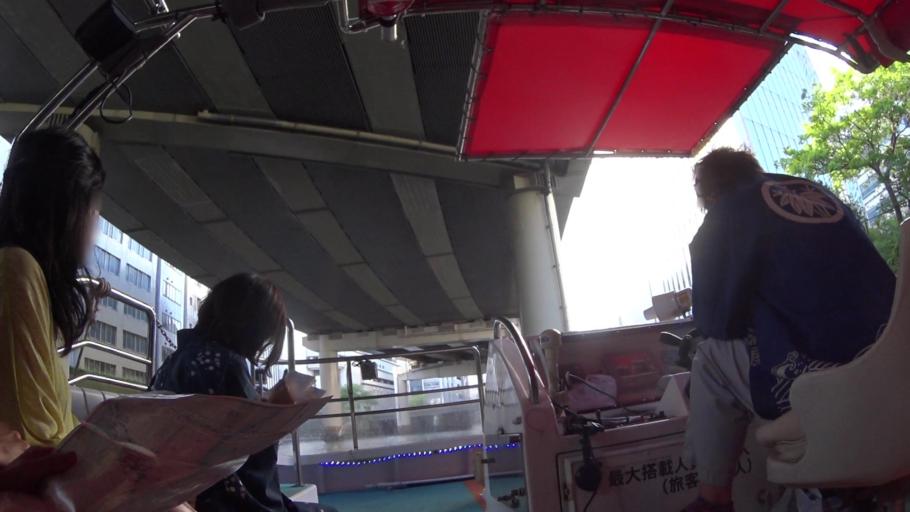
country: JP
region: Tokyo
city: Tokyo
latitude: 35.6814
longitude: 139.7810
